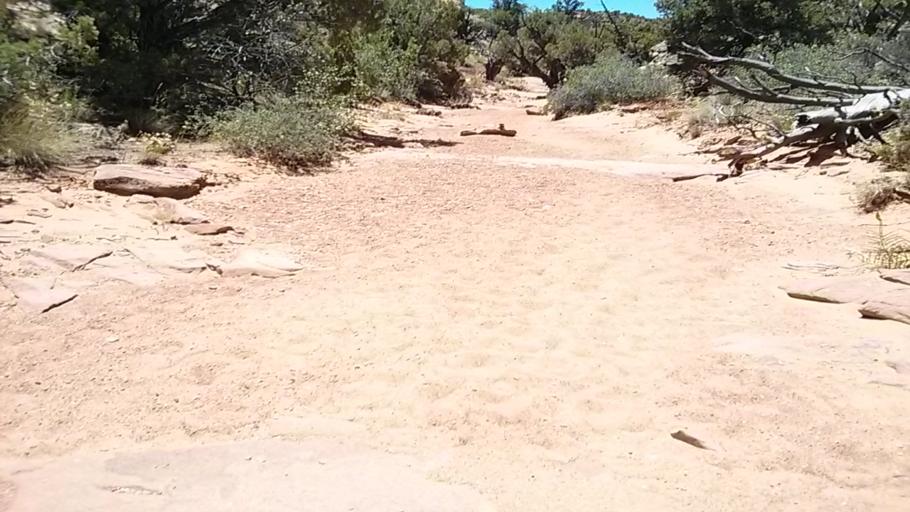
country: US
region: Utah
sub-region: Grand County
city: Moab
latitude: 38.4422
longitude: -109.9151
